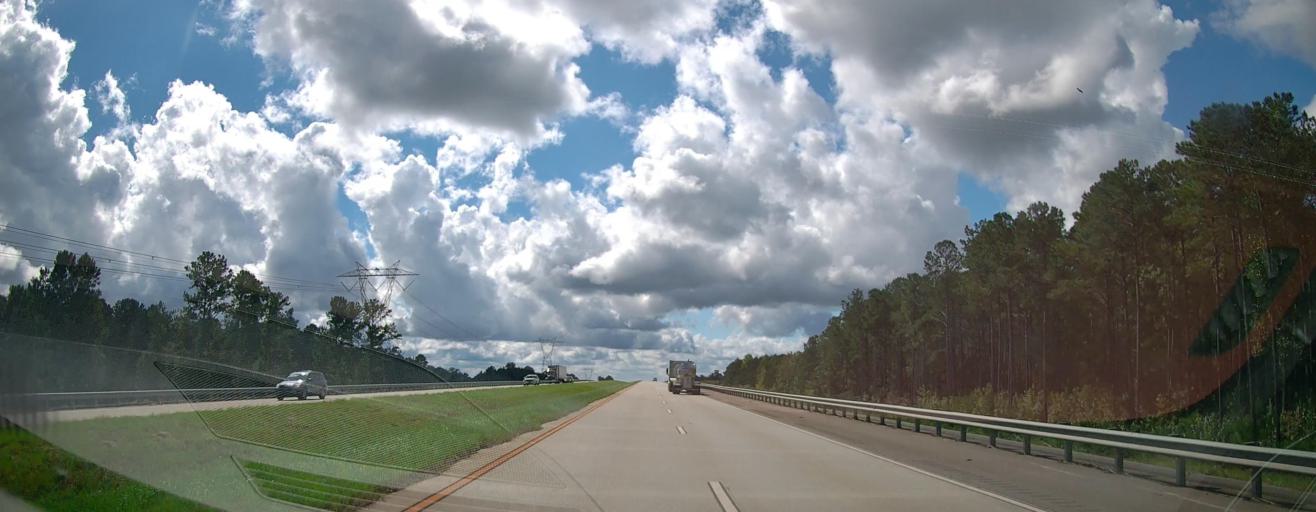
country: US
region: Georgia
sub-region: Jones County
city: Gray
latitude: 33.0245
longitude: -83.5524
